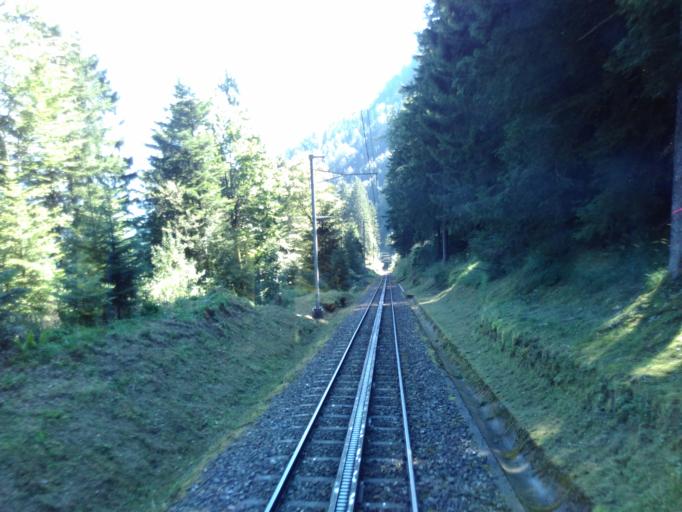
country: CH
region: Schwyz
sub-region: Bezirk Schwyz
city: Arth
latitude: 47.0382
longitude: 8.5100
